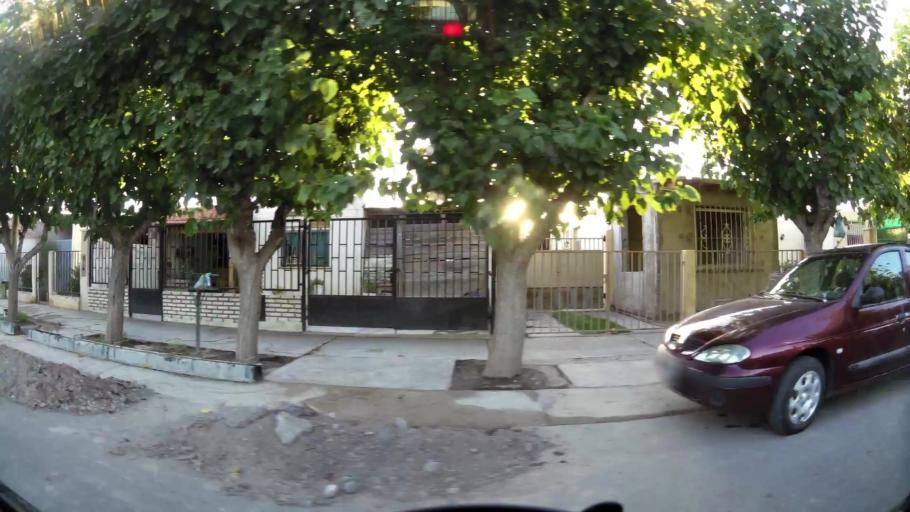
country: AR
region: San Juan
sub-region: Departamento de Santa Lucia
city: Santa Lucia
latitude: -31.5297
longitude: -68.5062
